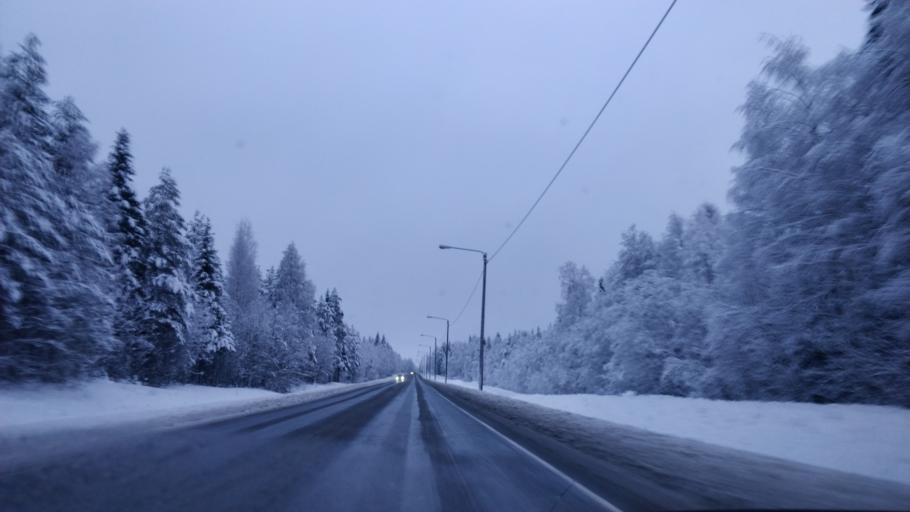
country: FI
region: Lapland
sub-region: Rovaniemi
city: Rovaniemi
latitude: 66.4560
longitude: 25.5840
